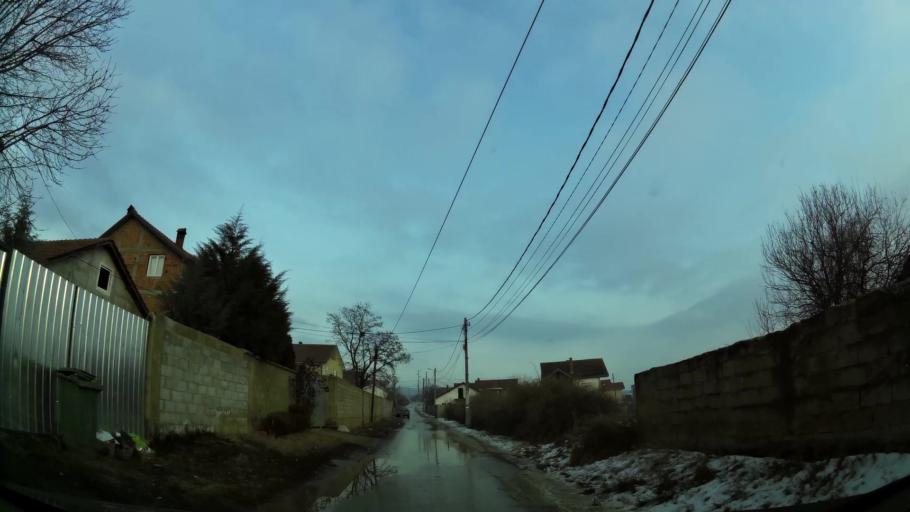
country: MK
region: Aracinovo
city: Arachinovo
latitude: 42.0224
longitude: 21.5713
